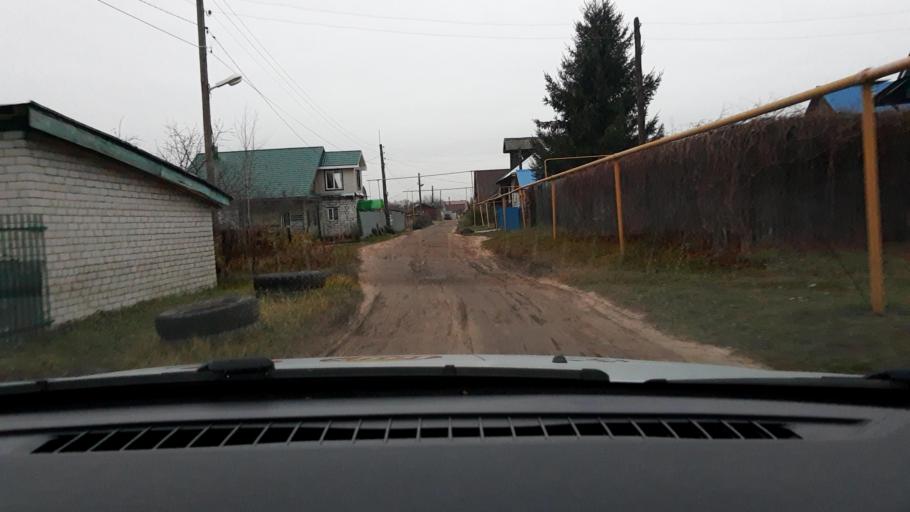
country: RU
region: Nizjnij Novgorod
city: Neklyudovo
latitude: 56.4232
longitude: 44.0151
